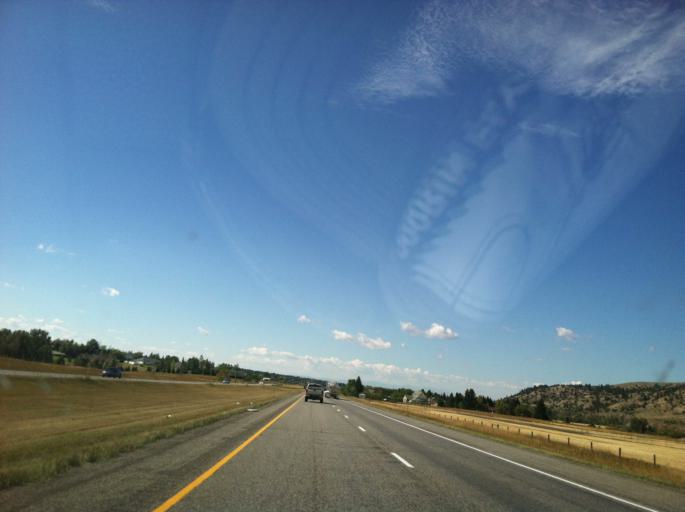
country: US
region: Montana
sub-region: Gallatin County
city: Bozeman
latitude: 45.6654
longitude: -110.9767
